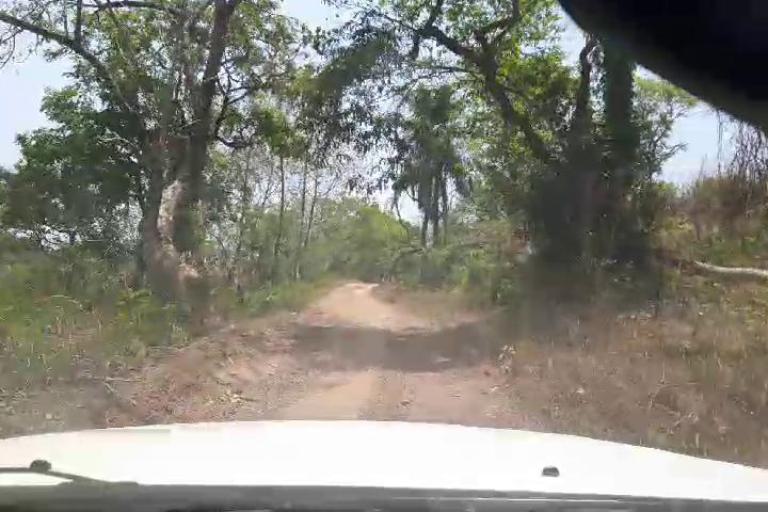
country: SL
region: Northern Province
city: Alikalia
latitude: 9.0782
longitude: -11.4717
